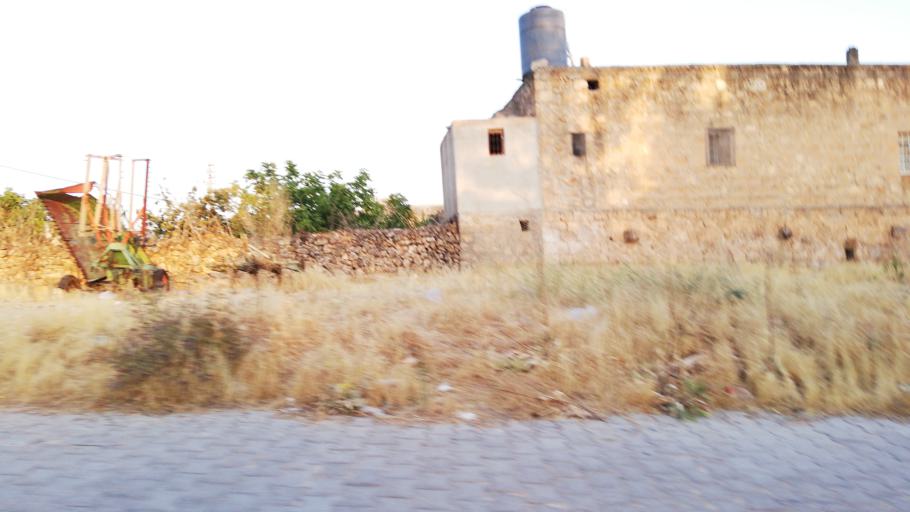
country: TR
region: Mardin
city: Kindirip
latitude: 37.4493
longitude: 41.2171
